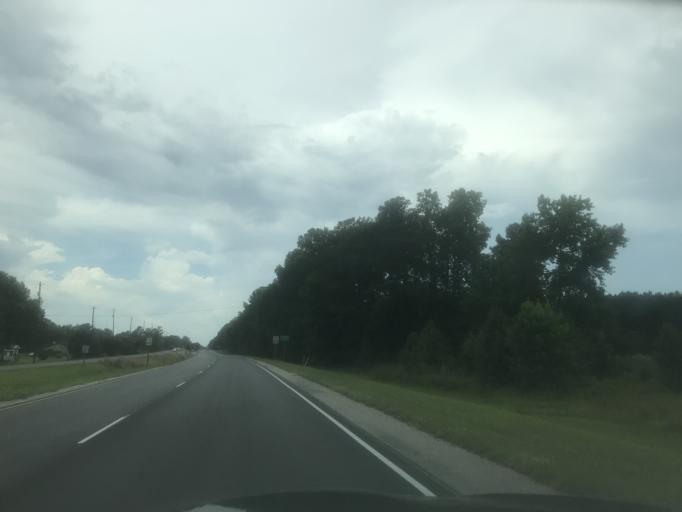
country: US
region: North Carolina
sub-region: Johnston County
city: Clayton
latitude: 35.6317
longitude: -78.4344
